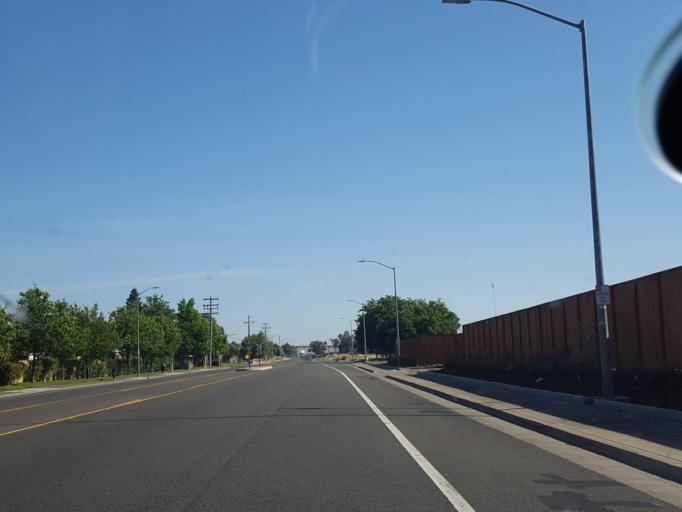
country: US
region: California
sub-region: Sacramento County
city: Florin
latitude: 38.4867
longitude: -121.3905
